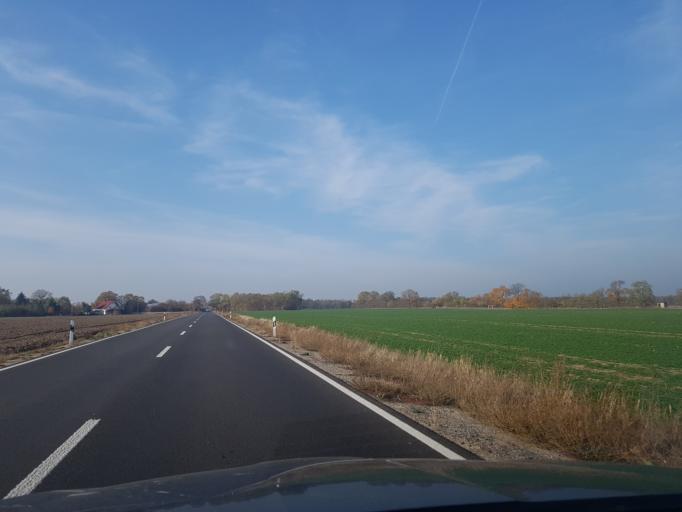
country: DE
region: Saxony
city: Arzberg
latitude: 51.5428
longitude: 13.1774
